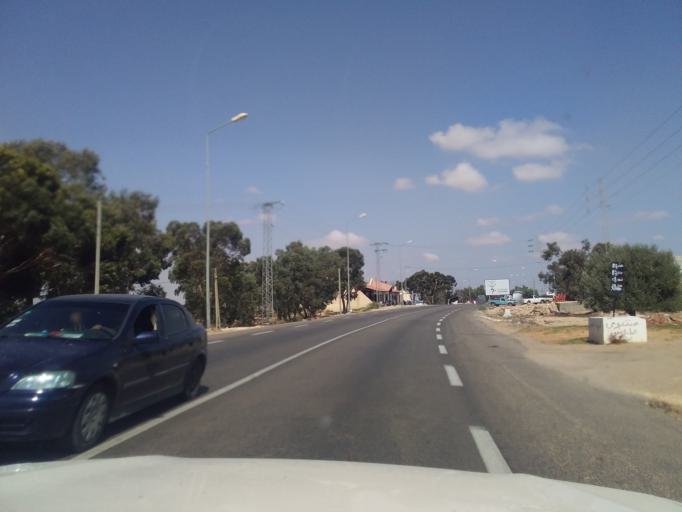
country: TN
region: Madanin
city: Medenine
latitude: 33.5889
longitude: 10.3150
